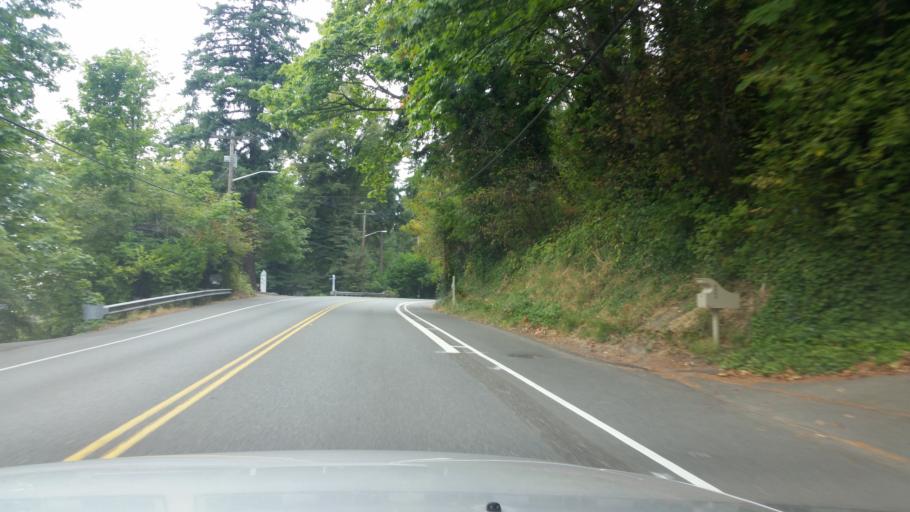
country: US
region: Washington
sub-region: King County
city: Inglewood-Finn Hill
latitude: 47.7035
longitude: -122.2231
